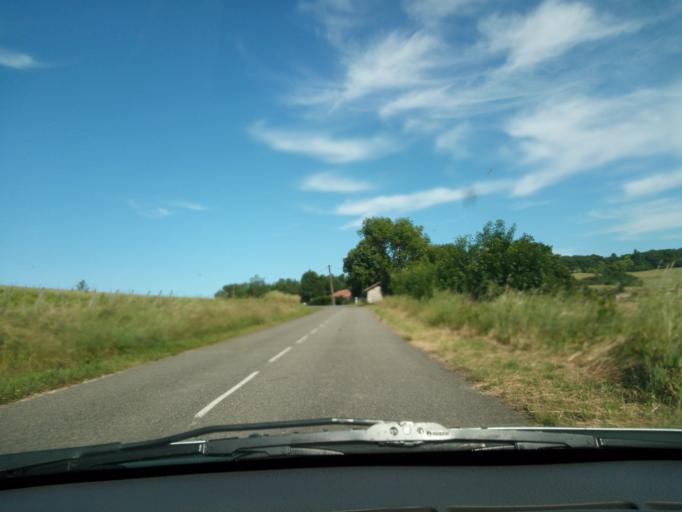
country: FR
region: Midi-Pyrenees
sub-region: Departement du Lot
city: Castelnau-Montratier
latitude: 44.2622
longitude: 1.3596
